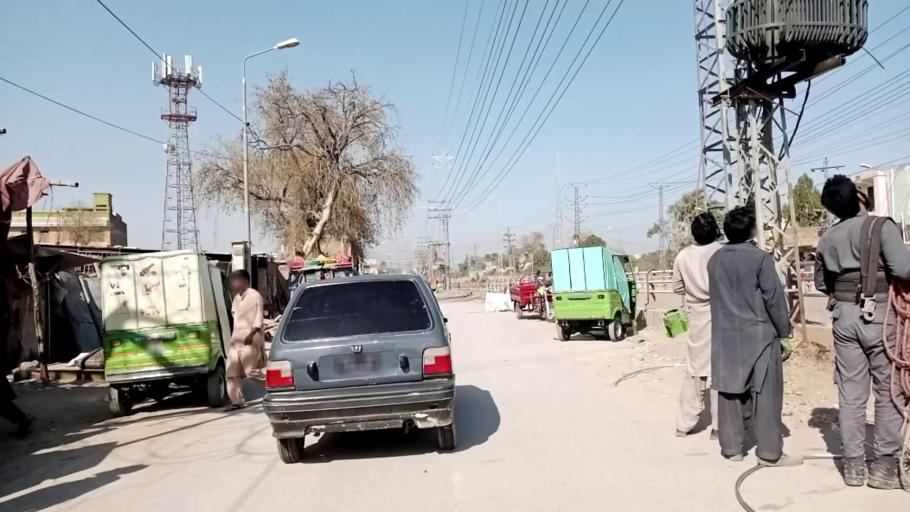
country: PK
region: Khyber Pakhtunkhwa
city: Peshawar
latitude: 33.9911
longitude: 71.4852
